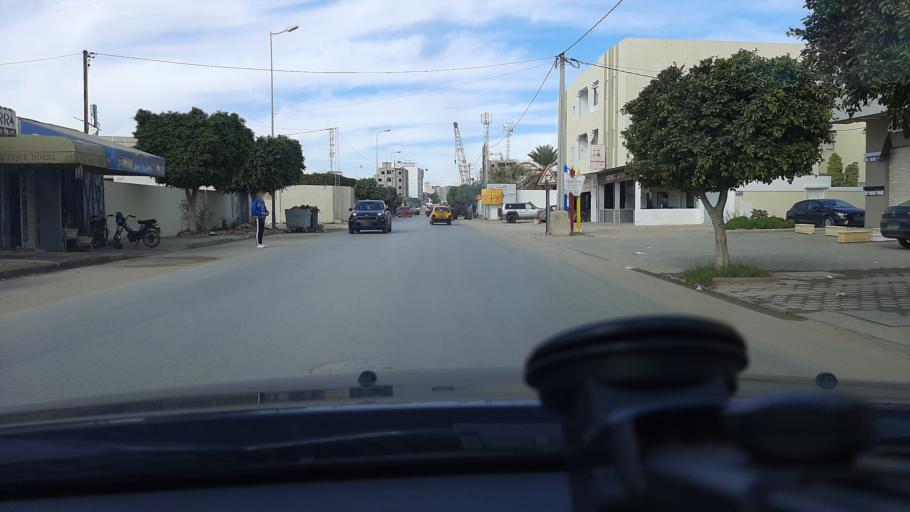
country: TN
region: Safaqis
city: Sfax
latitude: 34.7555
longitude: 10.7360
